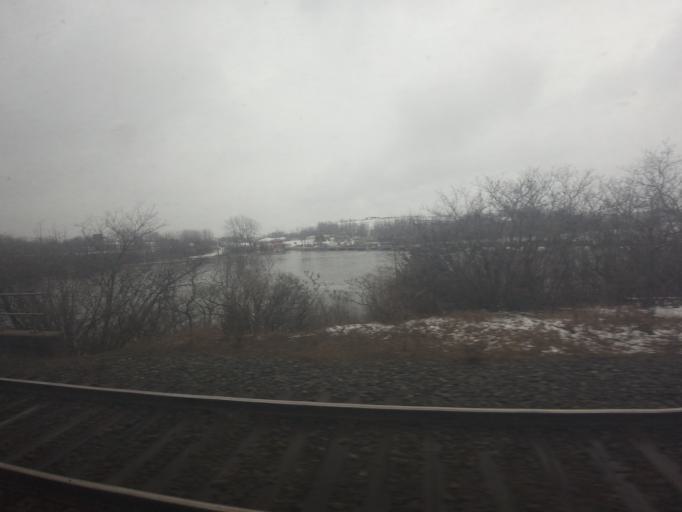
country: CA
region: Ontario
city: Quinte West
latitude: 44.1215
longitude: -77.5910
